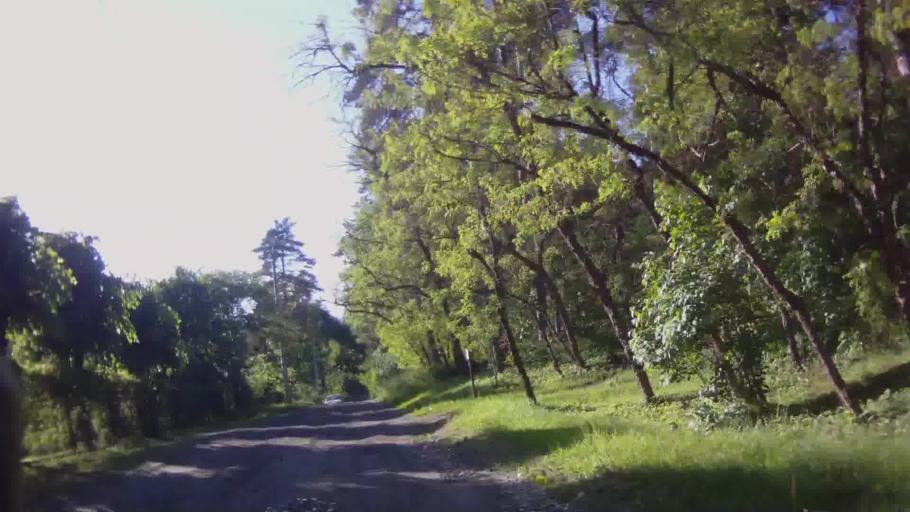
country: LV
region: Riga
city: Bergi
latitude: 56.9834
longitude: 24.3077
